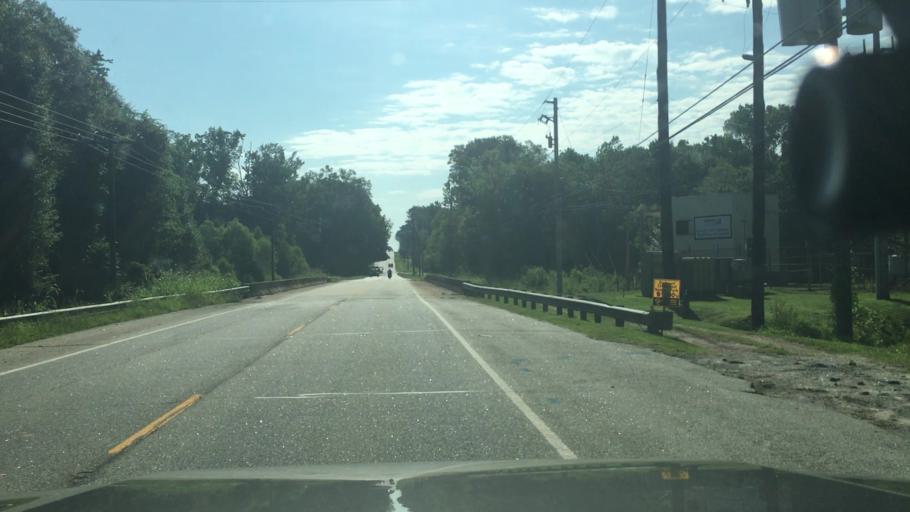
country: US
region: Georgia
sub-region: Coweta County
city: East Newnan
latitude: 33.3559
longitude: -84.7276
